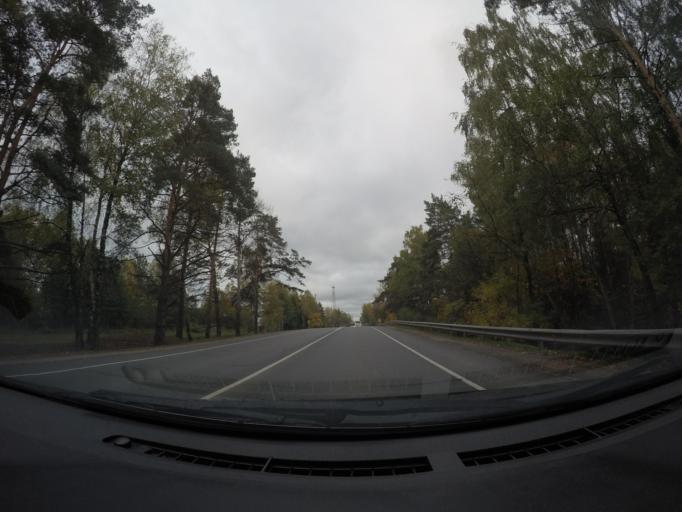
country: RU
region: Moskovskaya
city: Dorokhovo
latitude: 55.6372
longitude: 36.3296
